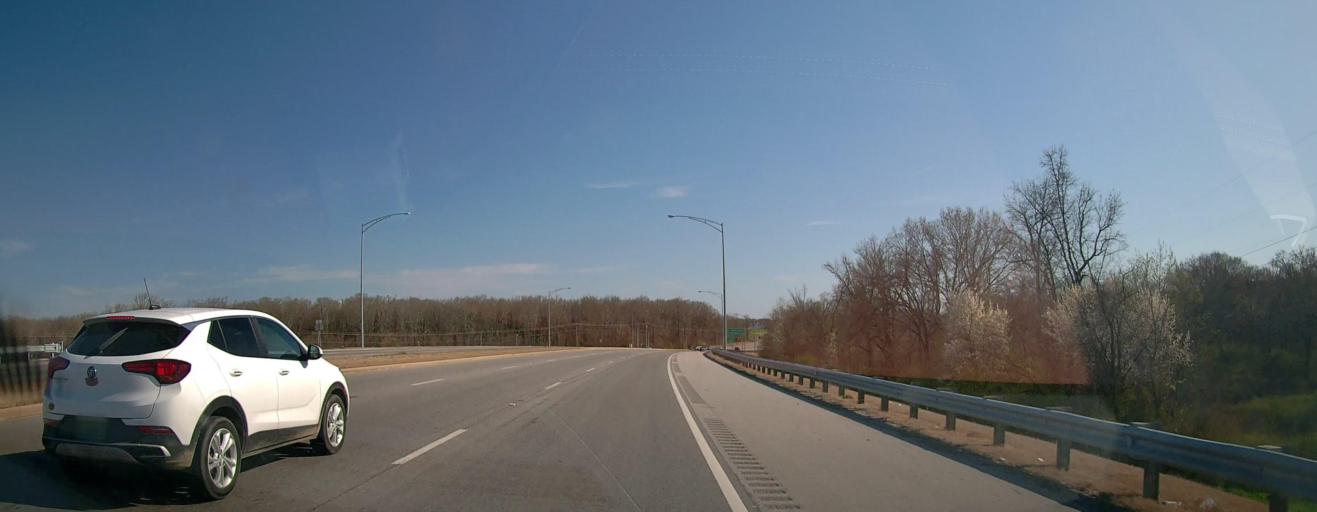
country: US
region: Alabama
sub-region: Lauderdale County
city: East Florence
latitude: 34.7814
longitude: -87.6350
